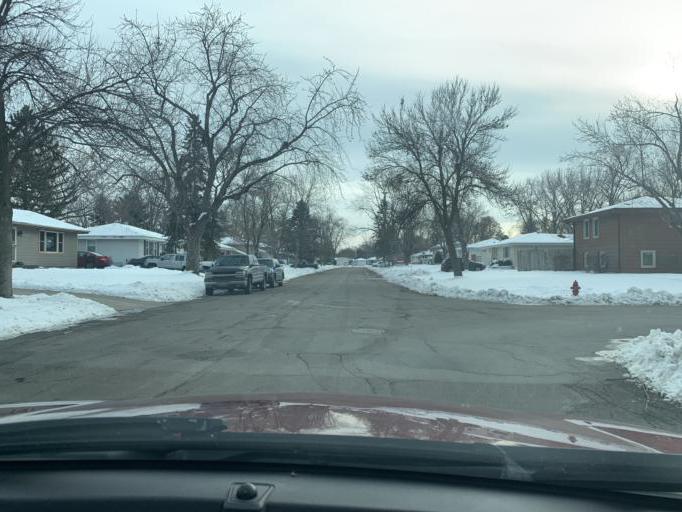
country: US
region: Minnesota
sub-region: Washington County
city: Saint Paul Park
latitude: 44.8359
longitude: -92.9754
